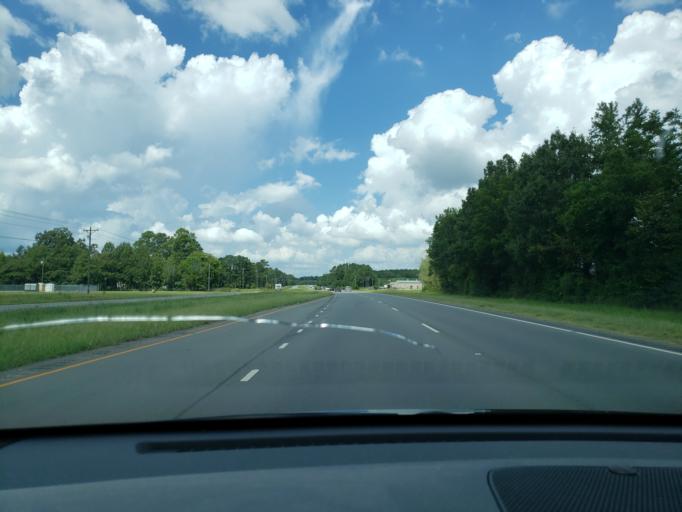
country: US
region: North Carolina
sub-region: Robeson County
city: Saint Pauls
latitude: 34.7597
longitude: -78.8052
